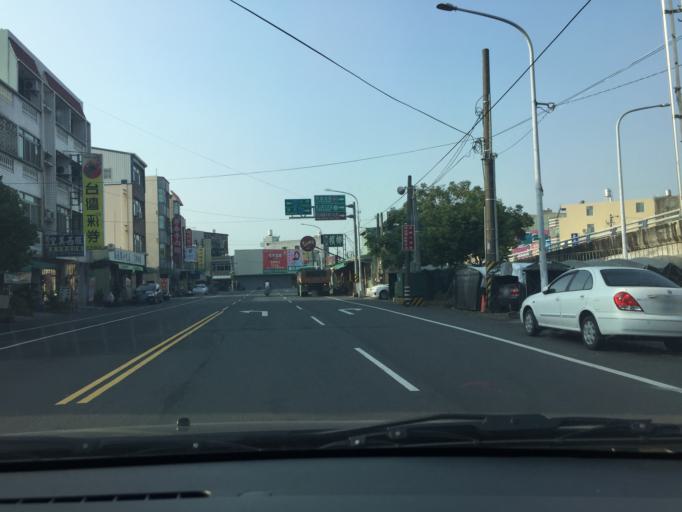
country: TW
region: Taiwan
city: Xinying
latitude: 23.1975
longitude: 120.3176
